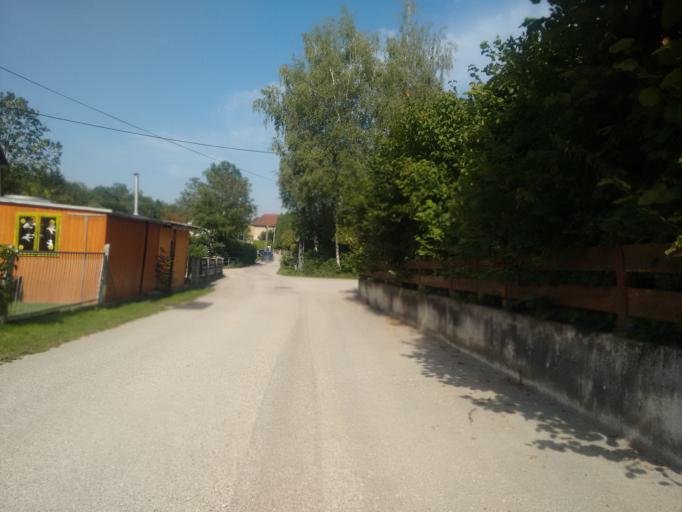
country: AT
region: Upper Austria
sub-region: Politischer Bezirk Grieskirchen
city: Bad Schallerbach
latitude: 48.2107
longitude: 13.9574
